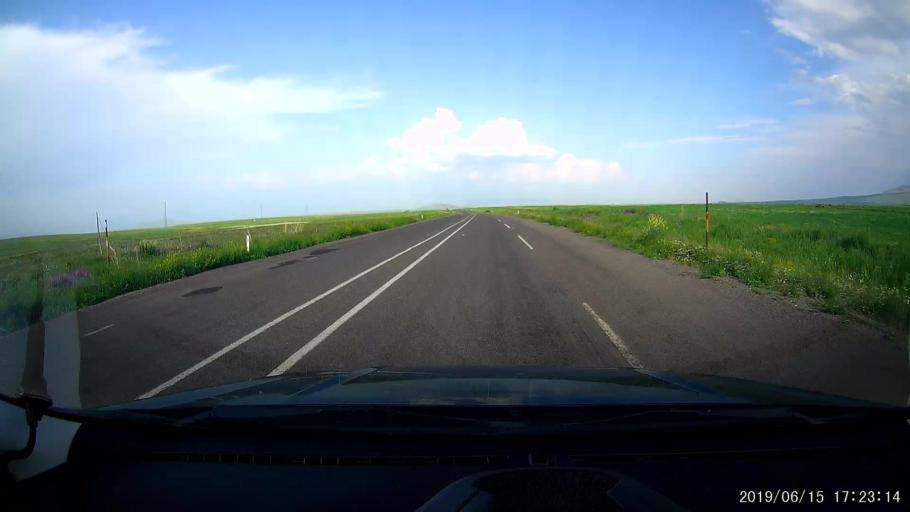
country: TR
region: Kars
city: Basgedikler
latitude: 40.6172
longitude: 43.3584
